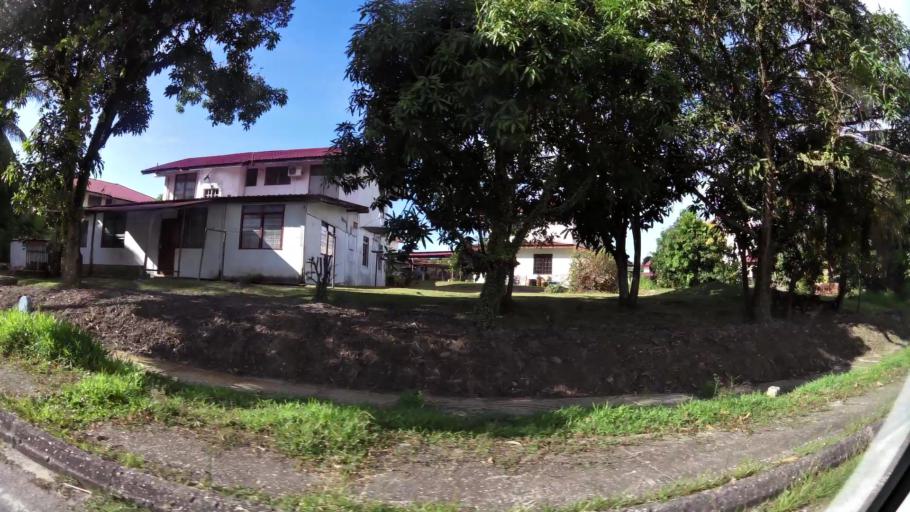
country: BN
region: Brunei and Muara
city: Bandar Seri Begawan
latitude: 4.9723
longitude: 114.9664
